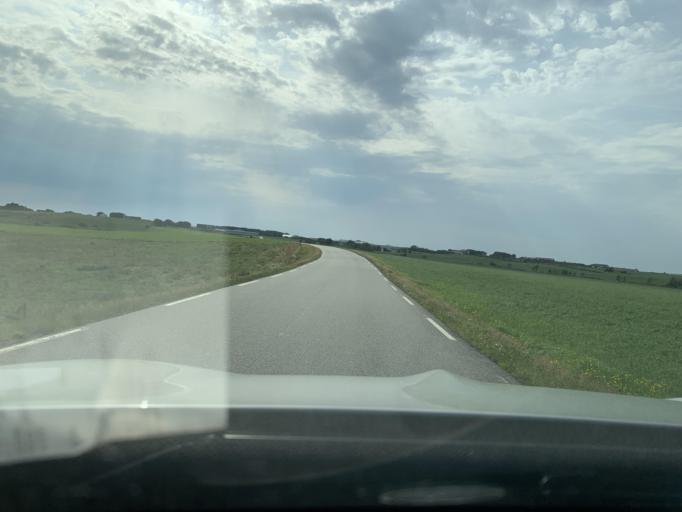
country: NO
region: Rogaland
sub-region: Klepp
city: Kleppe
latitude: 58.7191
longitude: 5.5610
